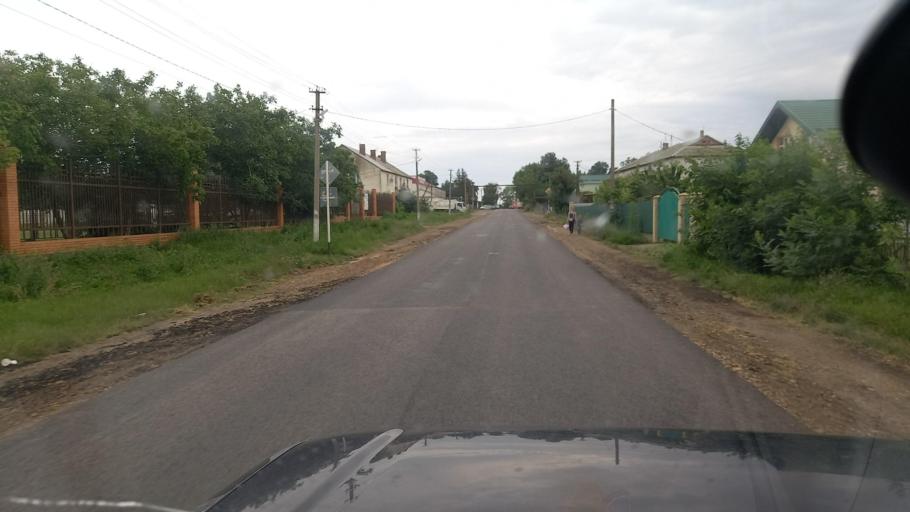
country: RU
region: Krasnodarskiy
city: Akhtanizovskaya
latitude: 45.3231
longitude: 37.1019
